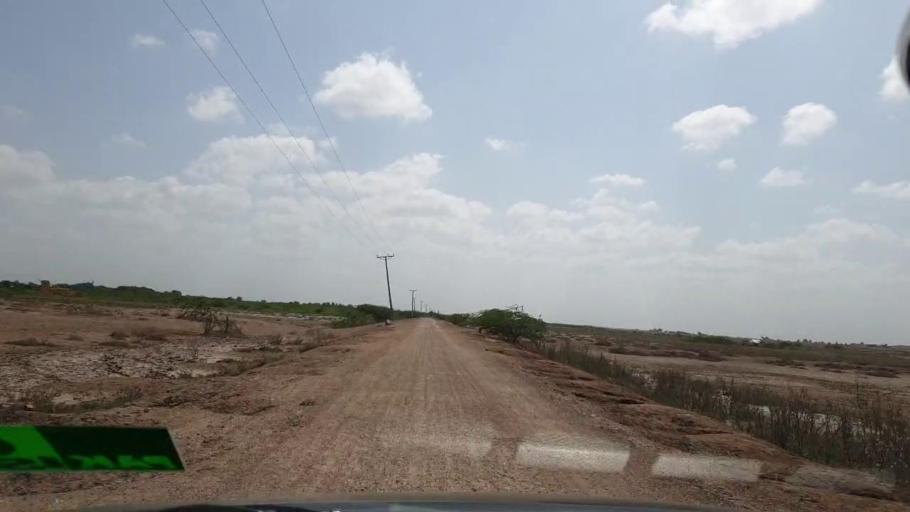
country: PK
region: Sindh
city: Kadhan
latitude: 24.6050
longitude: 69.1852
